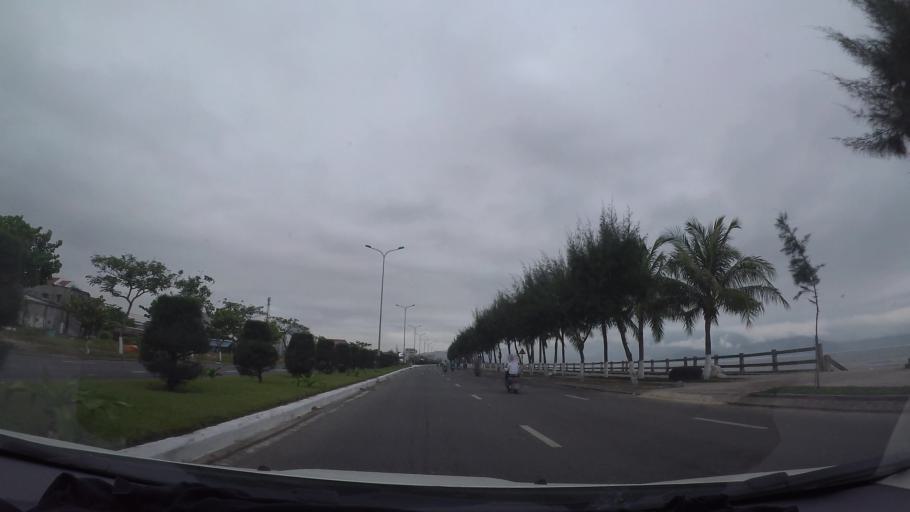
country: VN
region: Da Nang
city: Lien Chieu
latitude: 16.0837
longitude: 108.1622
